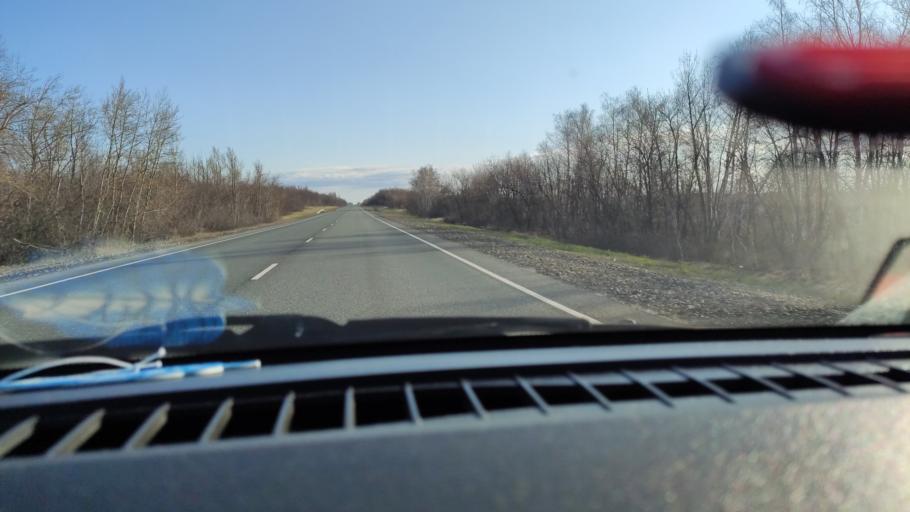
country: RU
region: Saratov
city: Khvalynsk
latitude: 52.5915
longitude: 48.1316
